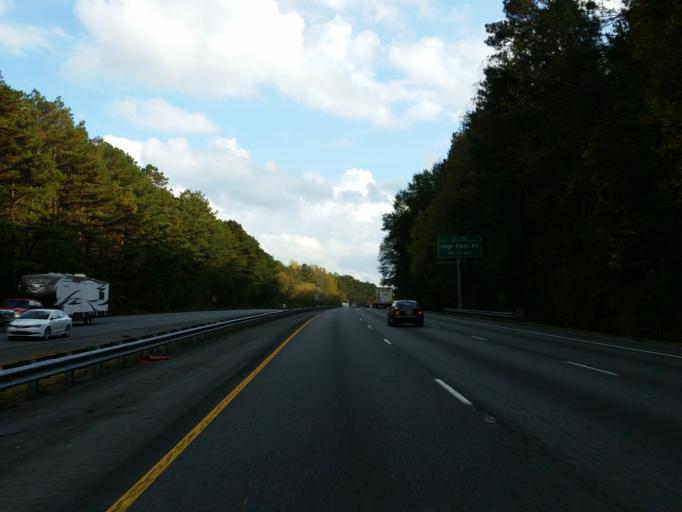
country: US
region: Georgia
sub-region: Butts County
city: Indian Springs
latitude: 33.1768
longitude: -84.0462
